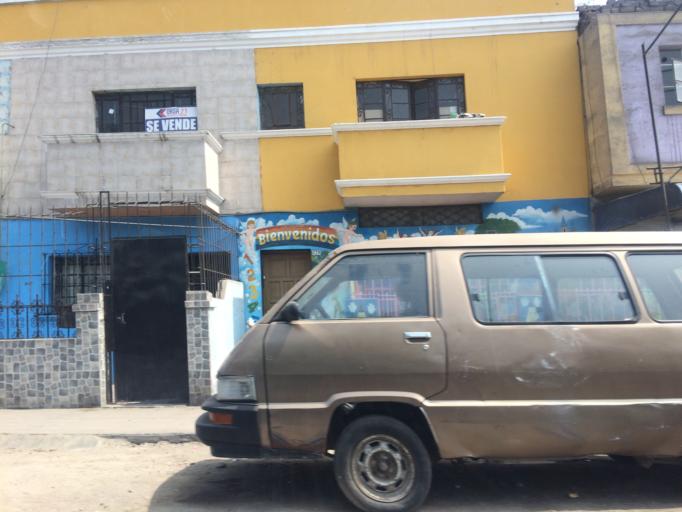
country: PE
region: Lima
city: Lima
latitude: -12.0320
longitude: -77.0375
